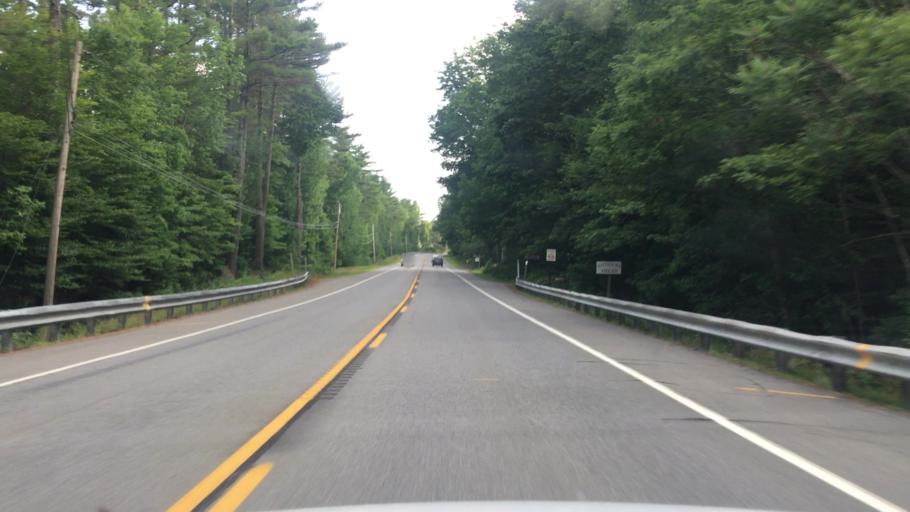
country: US
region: Maine
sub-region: Kennebec County
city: Windsor
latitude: 44.3558
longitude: -69.6442
